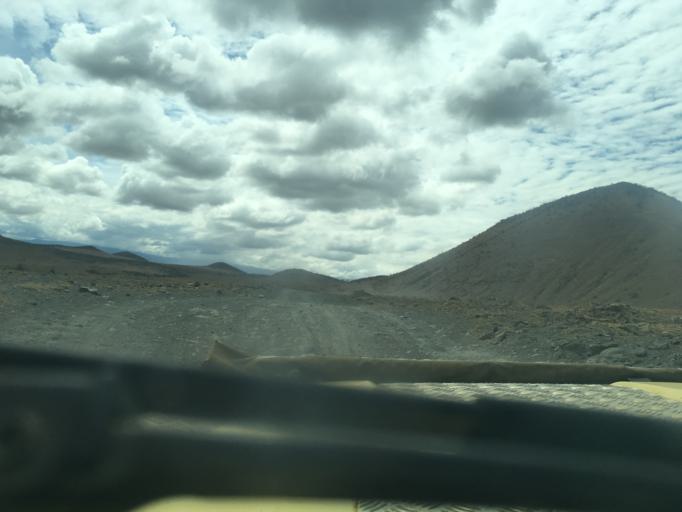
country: TZ
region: Arusha
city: Mto wa Mbu
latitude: -2.7420
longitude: 35.9742
